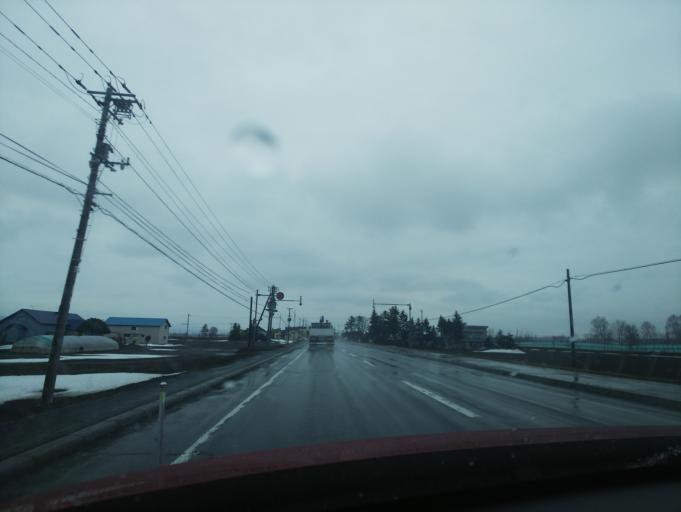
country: JP
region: Hokkaido
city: Nayoro
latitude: 44.2080
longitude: 142.3949
